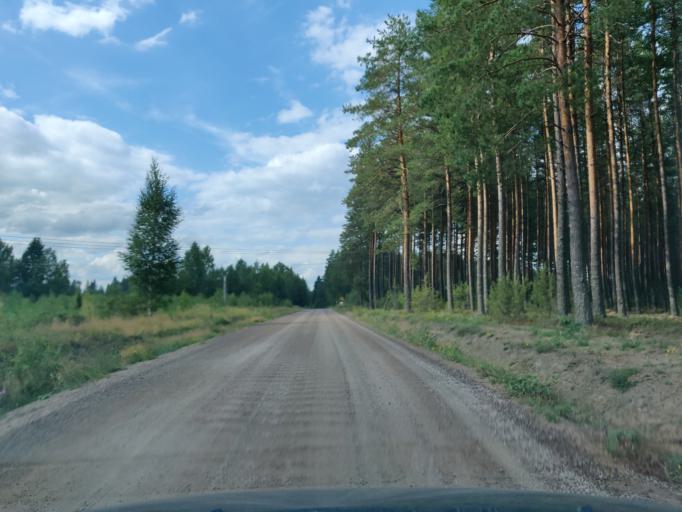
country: SE
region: Vaermland
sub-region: Munkfors Kommun
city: Munkfors
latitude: 59.9764
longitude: 13.5342
